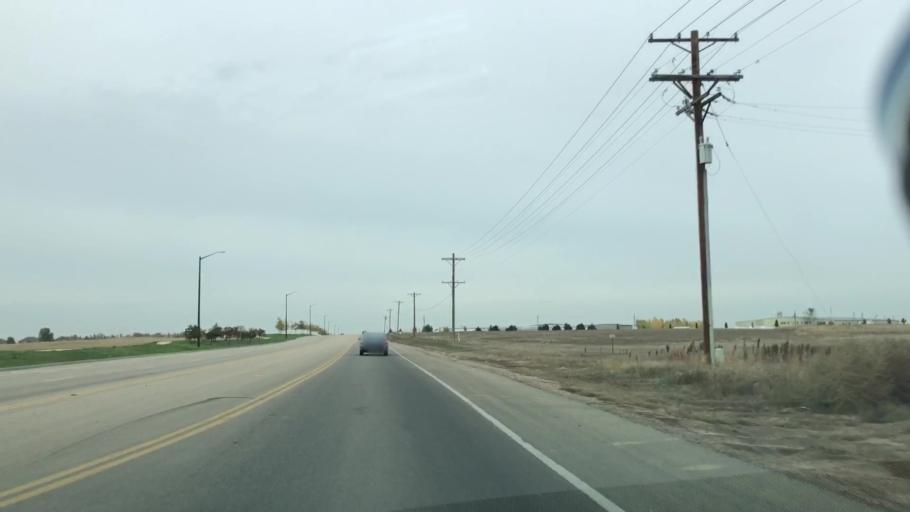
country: US
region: Colorado
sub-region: Larimer County
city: Loveland
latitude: 40.4361
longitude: -105.0204
